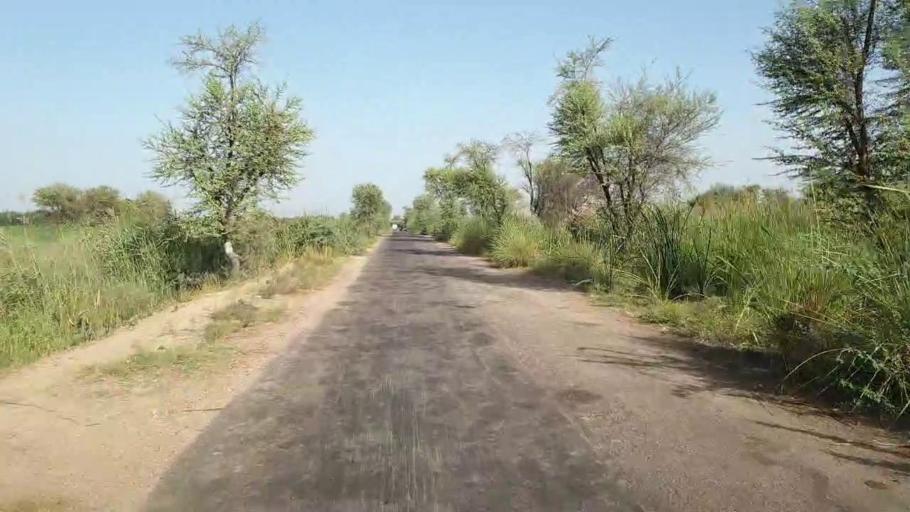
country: PK
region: Sindh
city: Nawabshah
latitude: 26.3777
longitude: 68.4612
